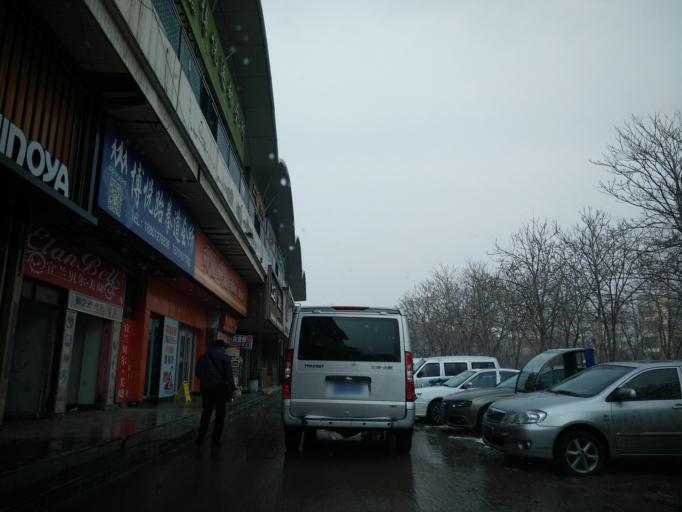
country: CN
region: Beijing
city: Jiugong
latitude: 39.7899
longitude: 116.4934
